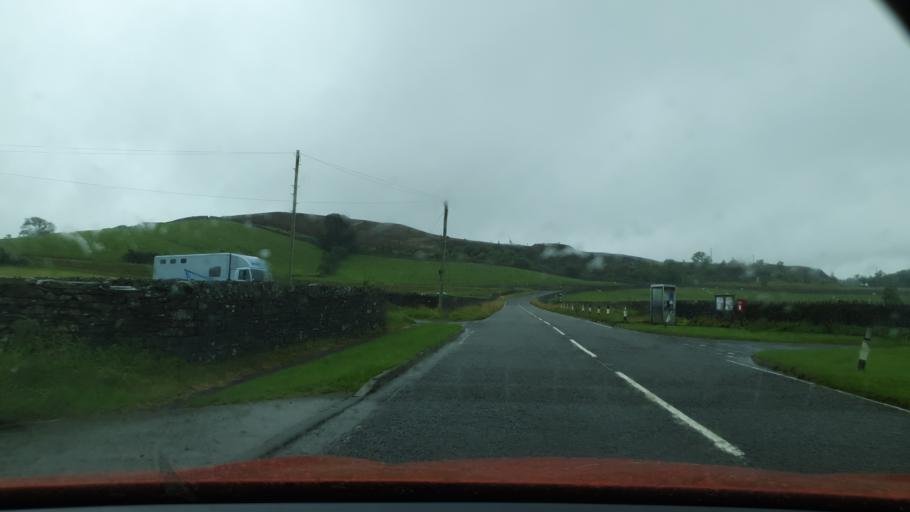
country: GB
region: England
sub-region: Cumbria
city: Ulverston
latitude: 54.2541
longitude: -3.1193
